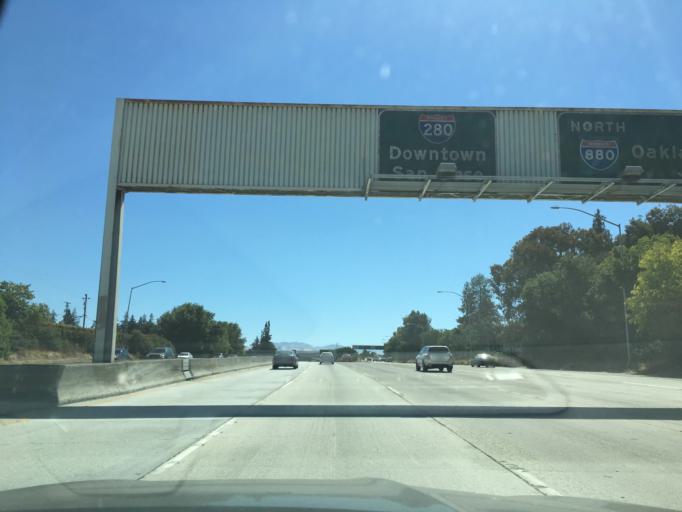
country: US
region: California
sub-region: Santa Clara County
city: Burbank
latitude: 37.3167
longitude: -121.9481
